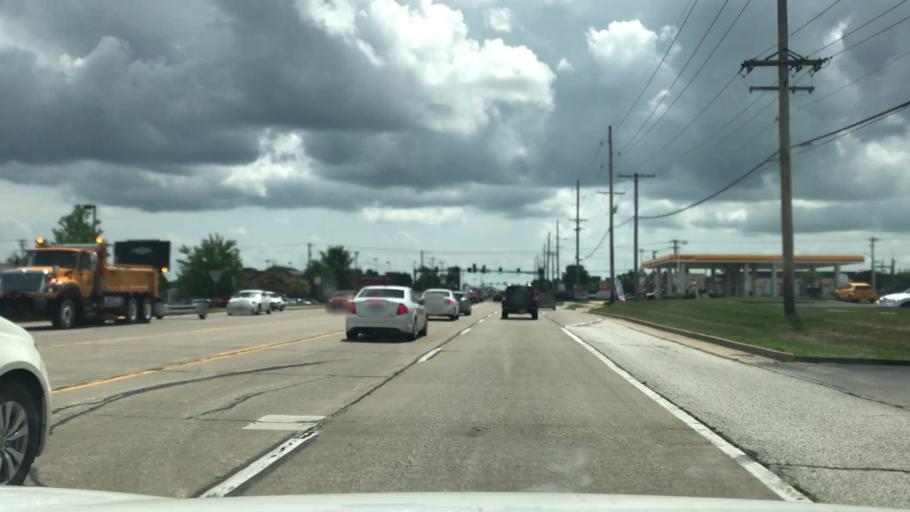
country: US
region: Missouri
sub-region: Saint Charles County
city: O'Fallon
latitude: 38.7817
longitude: -90.7000
